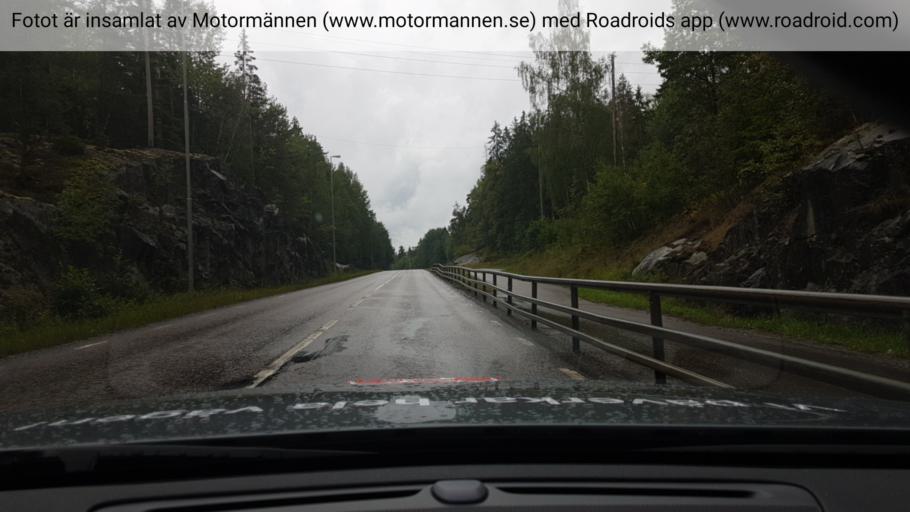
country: SE
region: Stockholm
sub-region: Botkyrka Kommun
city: Tullinge
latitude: 59.2053
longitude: 17.9245
